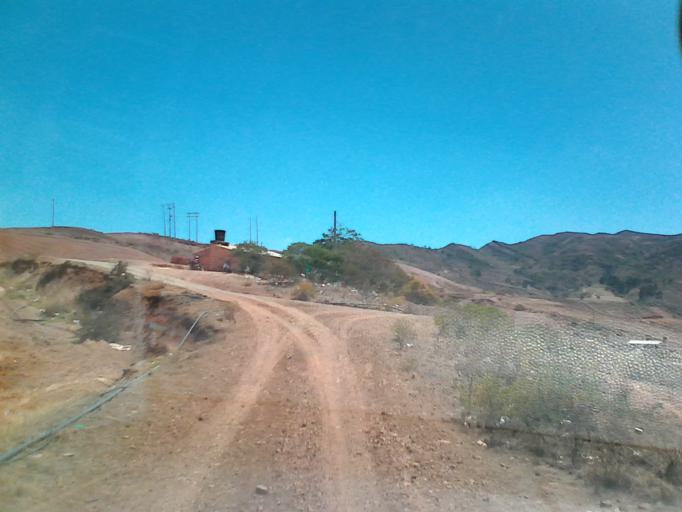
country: CO
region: Boyaca
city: Sachica
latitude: 5.5926
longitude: -73.5643
